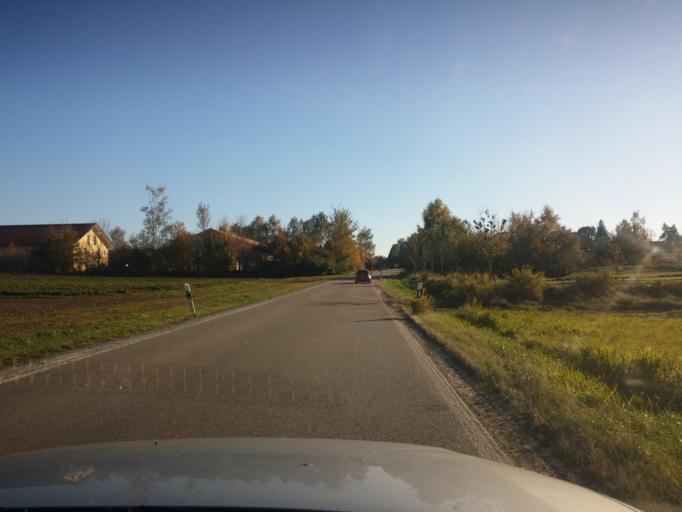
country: DE
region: Bavaria
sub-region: Upper Bavaria
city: Egmating
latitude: 48.0074
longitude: 11.8001
